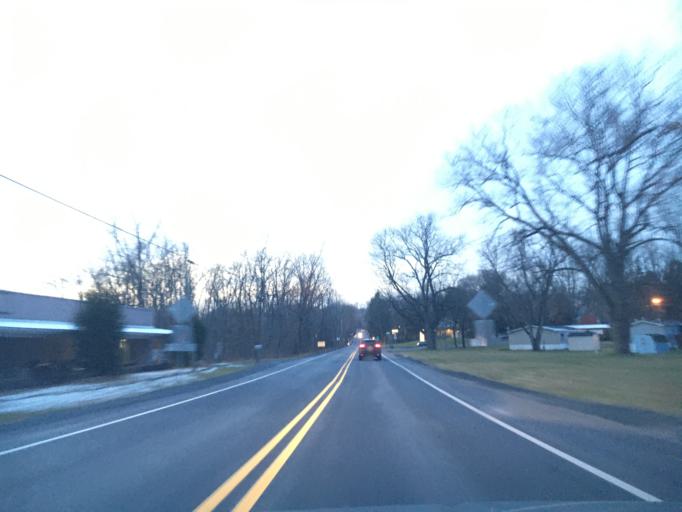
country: US
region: Pennsylvania
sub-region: Northampton County
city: Youngsville
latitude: 40.7496
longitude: -75.4743
